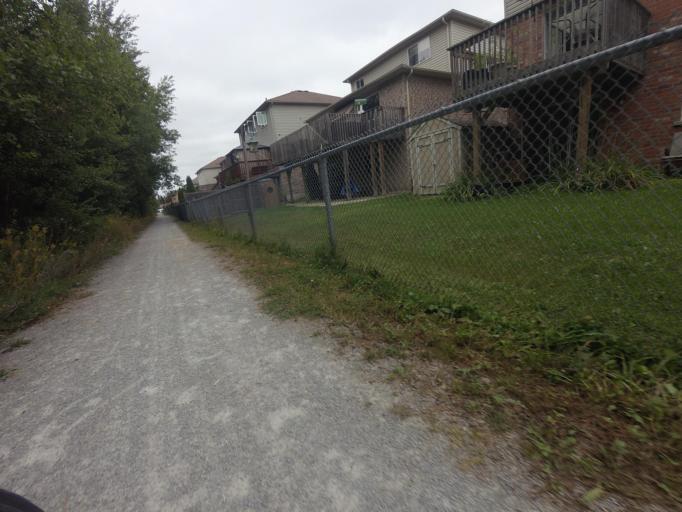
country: CA
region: Ontario
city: Omemee
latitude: 44.3361
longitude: -78.7512
